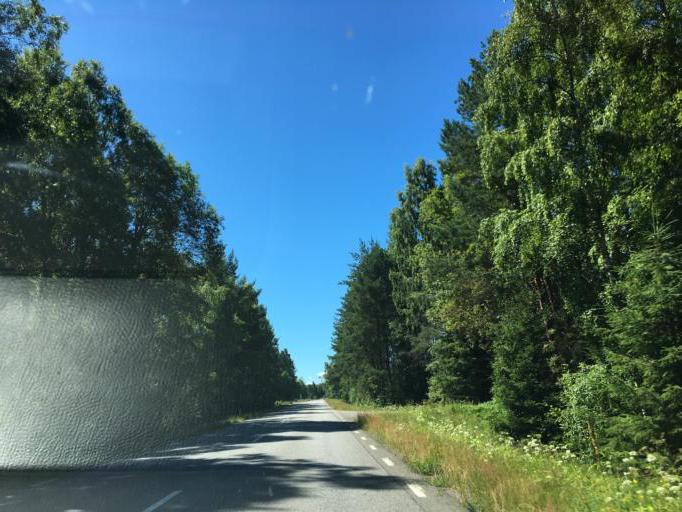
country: SE
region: OErebro
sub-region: Laxa Kommun
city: Laxa
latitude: 58.8135
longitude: 14.5493
